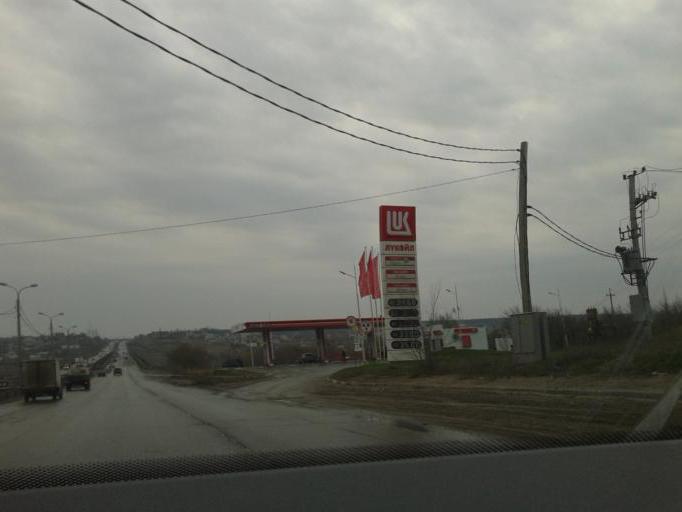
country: RU
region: Volgograd
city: Volgograd
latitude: 48.7207
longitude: 44.4454
